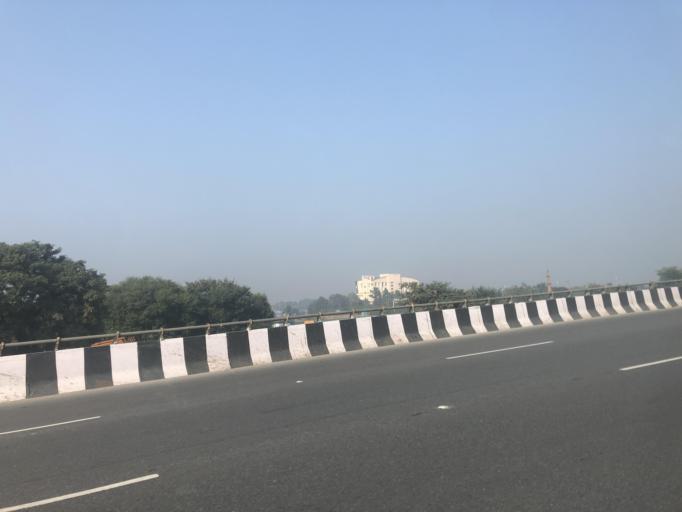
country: IN
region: Haryana
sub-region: Gurgaon
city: Gurgaon
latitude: 28.5418
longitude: 77.1177
